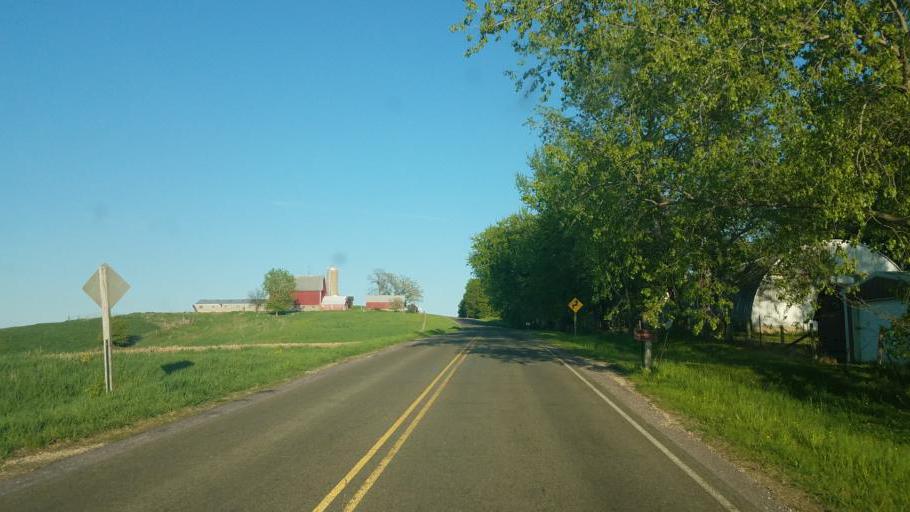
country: US
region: Wisconsin
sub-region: Vernon County
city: Hillsboro
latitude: 43.6519
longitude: -90.2971
